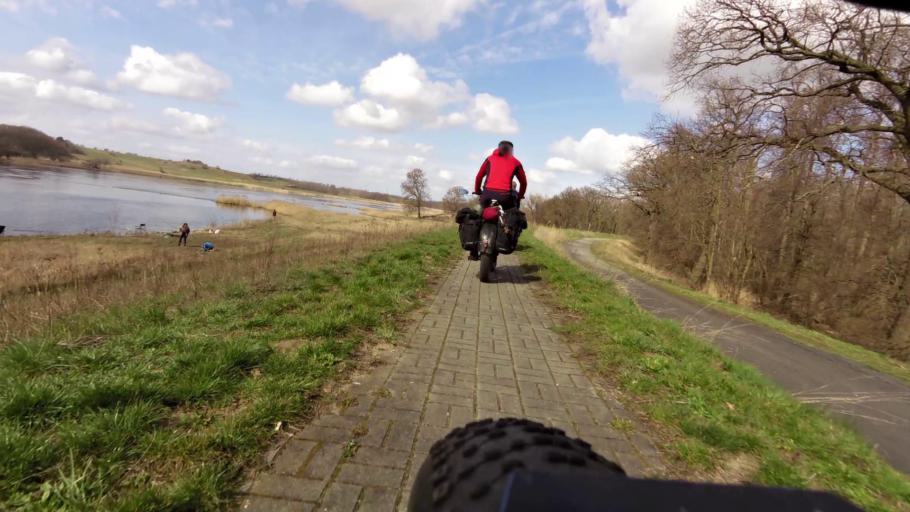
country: DE
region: Brandenburg
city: Lebus
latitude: 52.3905
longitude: 14.5400
